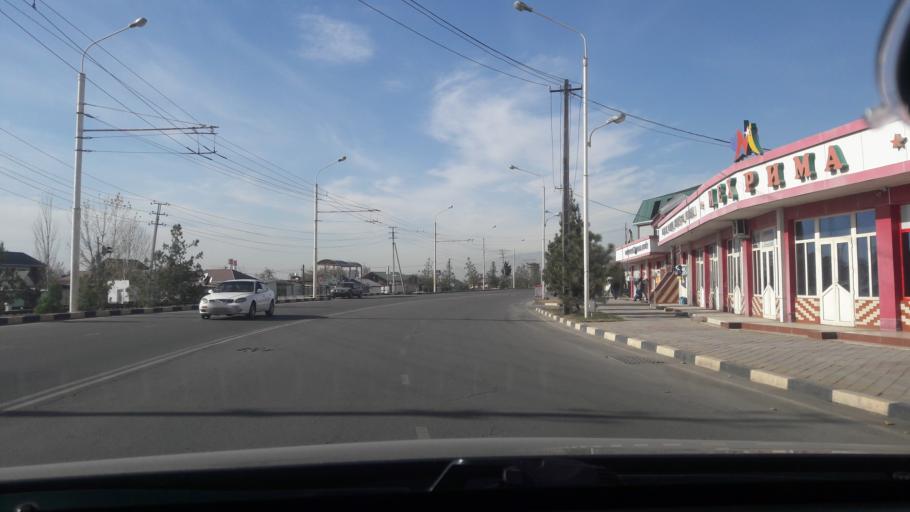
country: TJ
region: Dushanbe
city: Dushanbe
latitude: 38.5573
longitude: 68.7892
